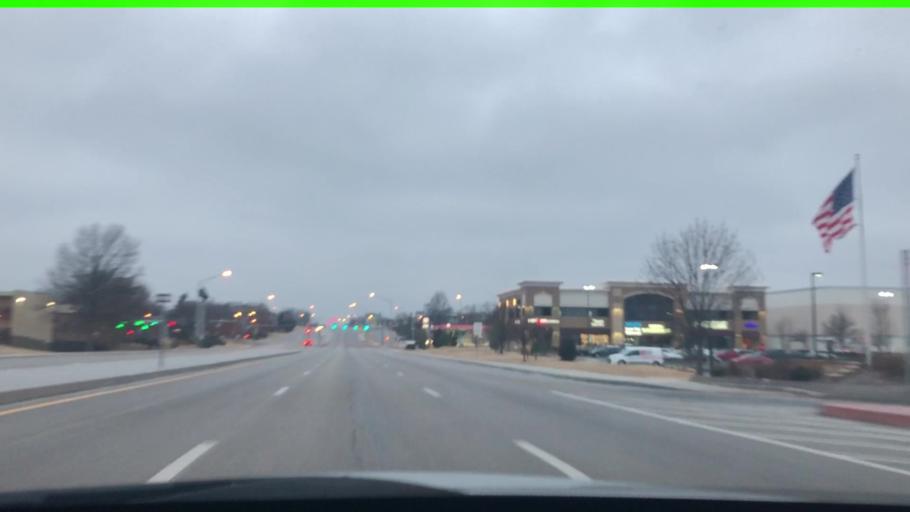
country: US
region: Missouri
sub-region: Boone County
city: Columbia
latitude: 38.9598
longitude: -92.3714
